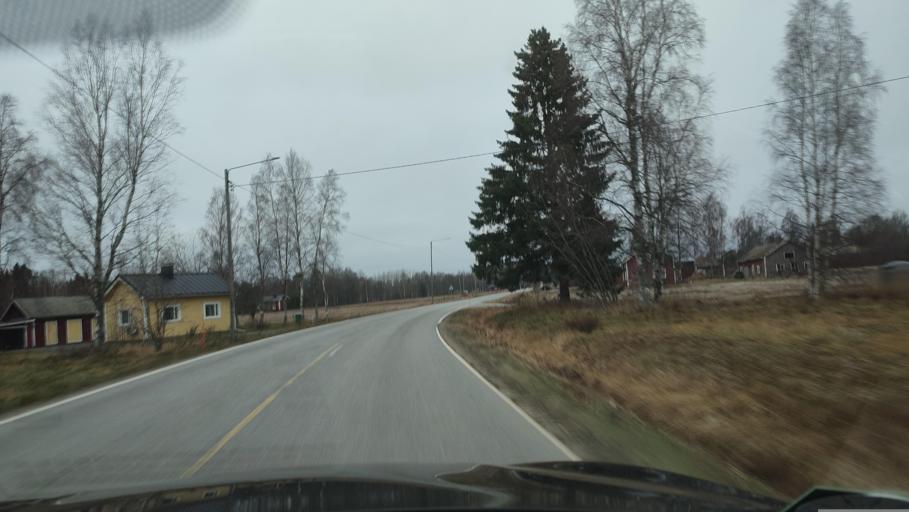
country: FI
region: Southern Ostrobothnia
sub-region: Suupohja
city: Karijoki
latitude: 62.2721
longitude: 21.7082
